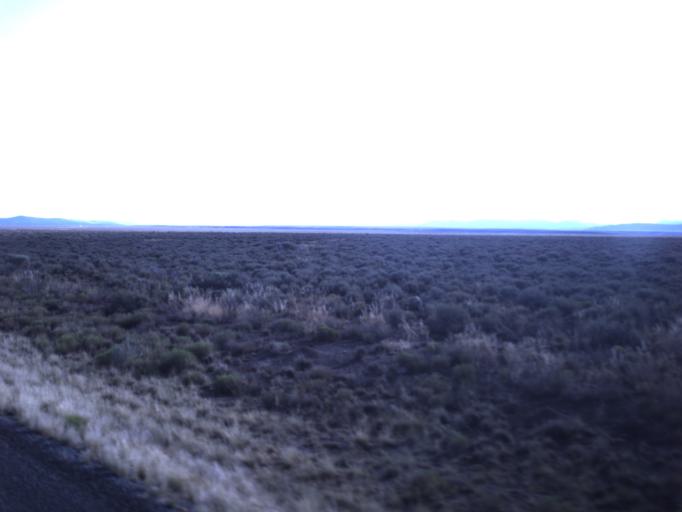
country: US
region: Utah
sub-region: Iron County
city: Enoch
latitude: 37.9191
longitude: -113.0315
